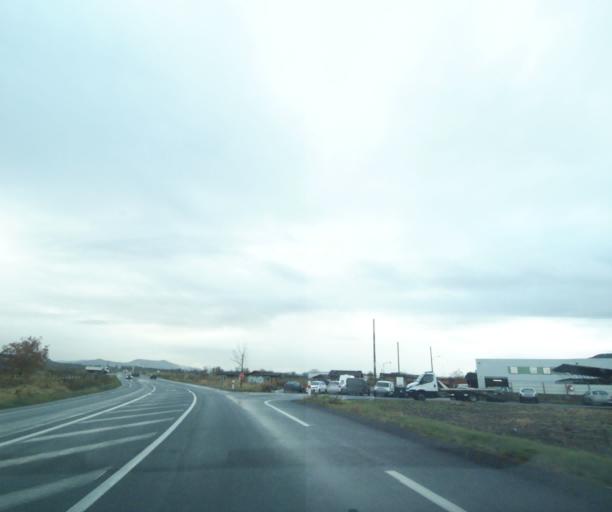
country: FR
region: Auvergne
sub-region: Departement du Puy-de-Dome
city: Perignat-les-Sarlieve
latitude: 45.7622
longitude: 3.1502
